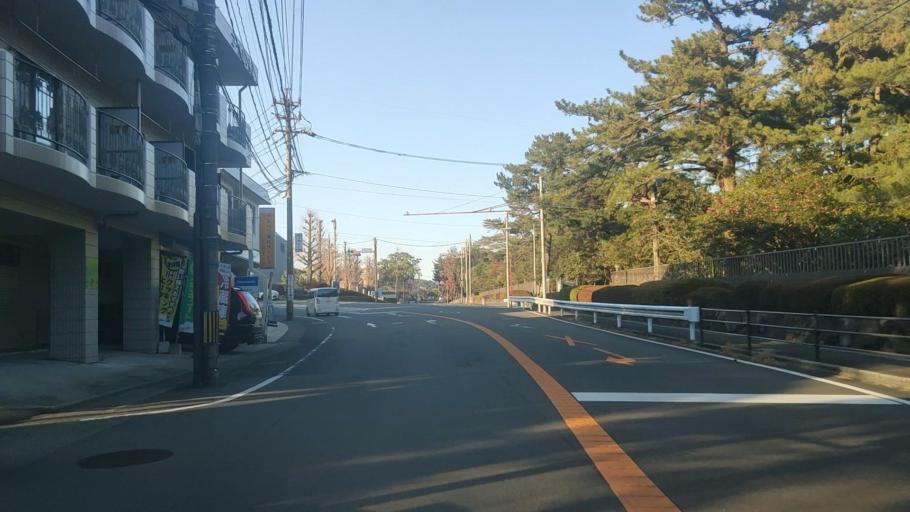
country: JP
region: Oita
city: Beppu
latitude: 33.2810
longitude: 131.4890
